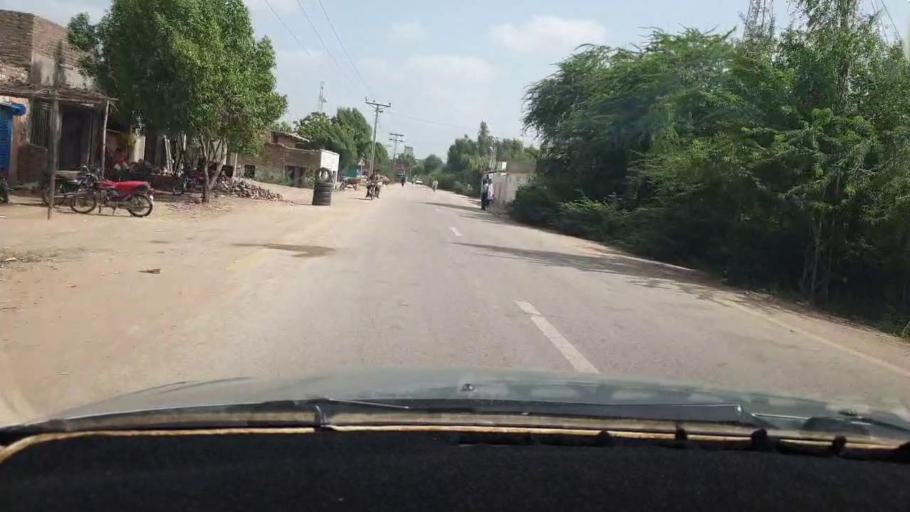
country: PK
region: Sindh
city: Digri
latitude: 25.0757
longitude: 69.2122
